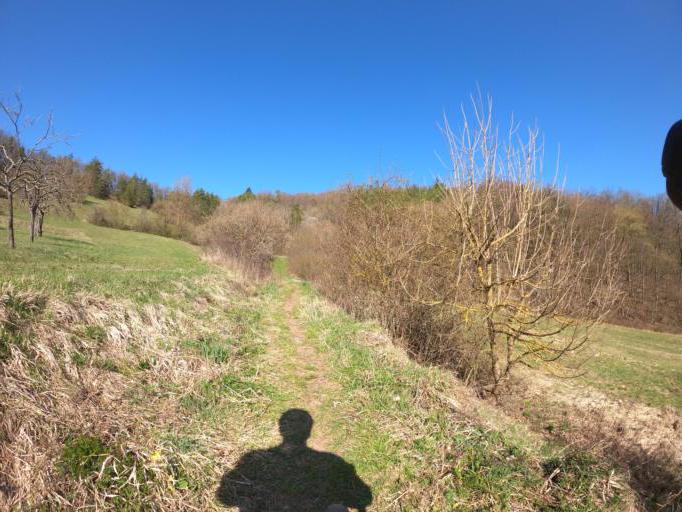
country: DE
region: Baden-Wuerttemberg
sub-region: Tuebingen Region
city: Rottenburg
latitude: 48.4461
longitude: 8.9349
